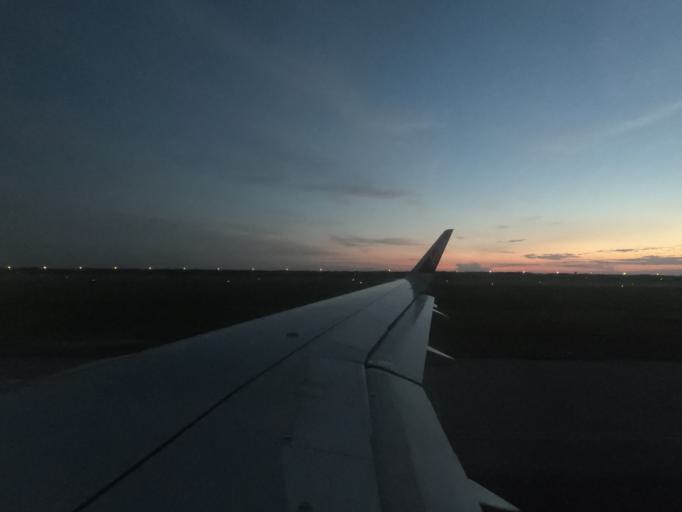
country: MY
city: Sungai Pelek New Village
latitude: 2.7143
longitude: 101.6955
